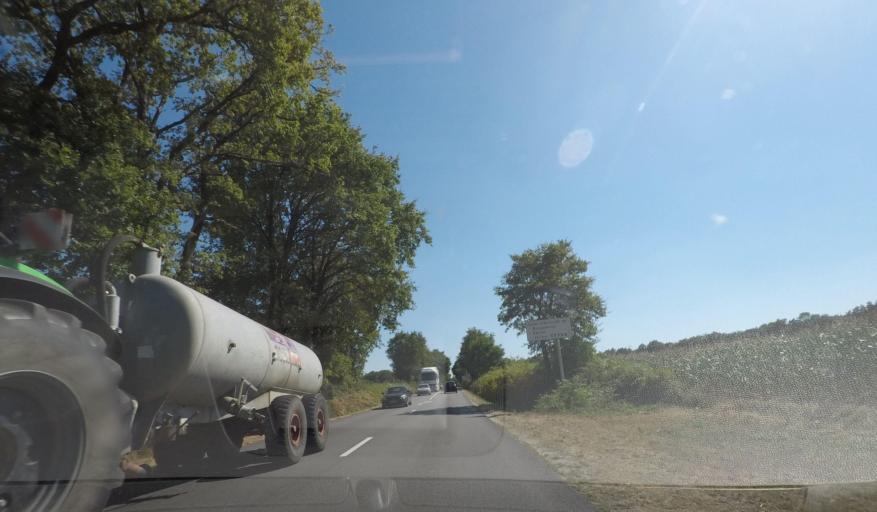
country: FR
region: Brittany
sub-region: Departement du Morbihan
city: Questembert
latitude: 47.6907
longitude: -2.4482
